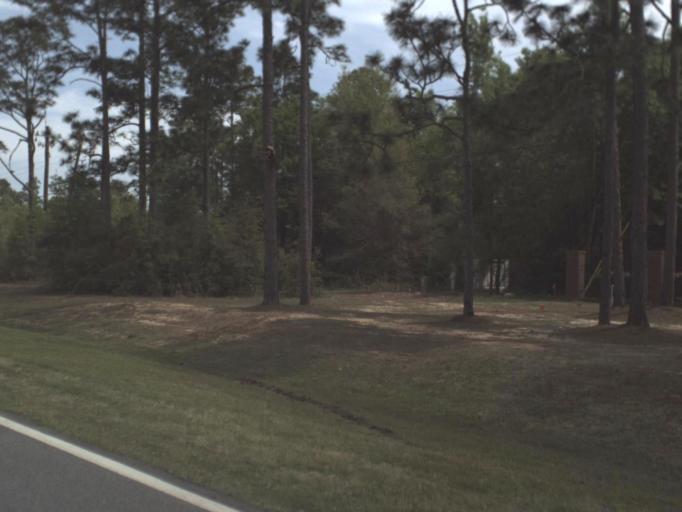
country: US
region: Florida
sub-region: Escambia County
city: Cantonment
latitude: 30.5352
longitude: -87.3639
